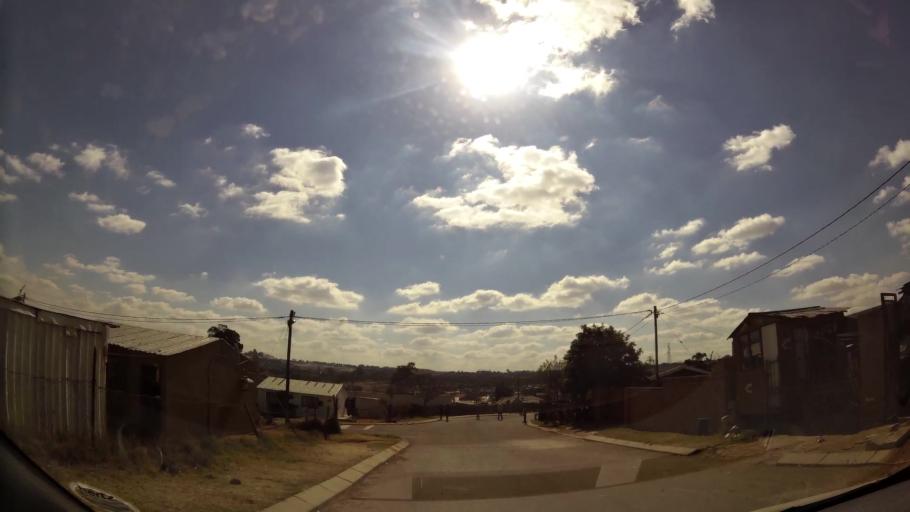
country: ZA
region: Gauteng
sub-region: West Rand District Municipality
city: Krugersdorp
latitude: -26.1420
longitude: 27.7830
